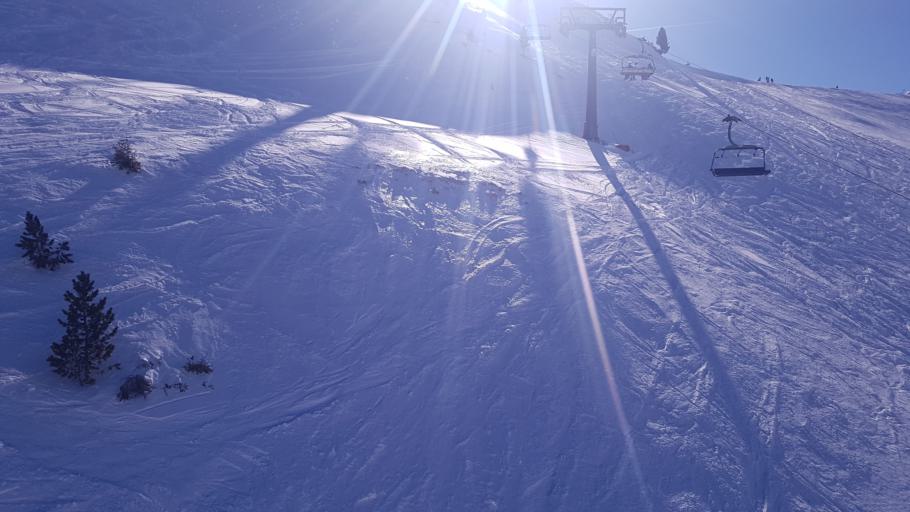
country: AT
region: Salzburg
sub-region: Politischer Bezirk Zell am See
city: Neukirchen am Grossvenediger
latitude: 47.2876
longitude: 12.2865
